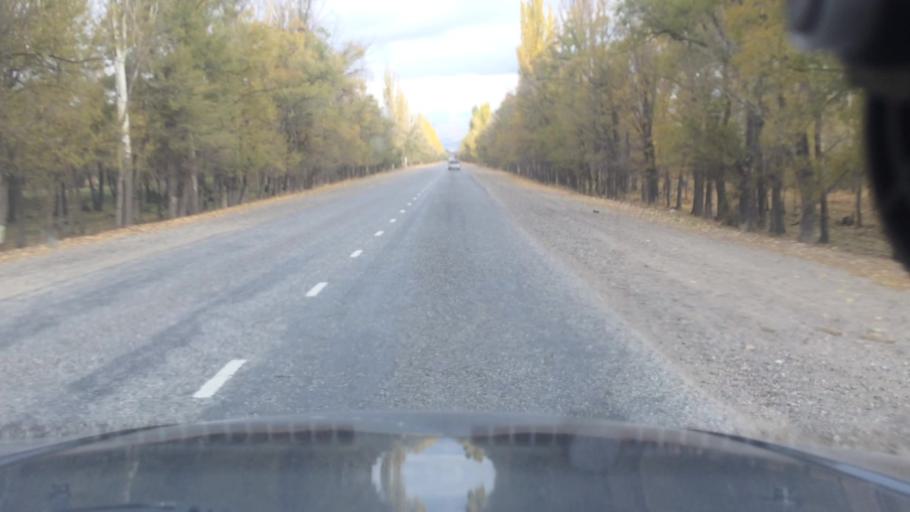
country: KG
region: Ysyk-Koel
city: Tyup
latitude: 42.6319
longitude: 78.3602
